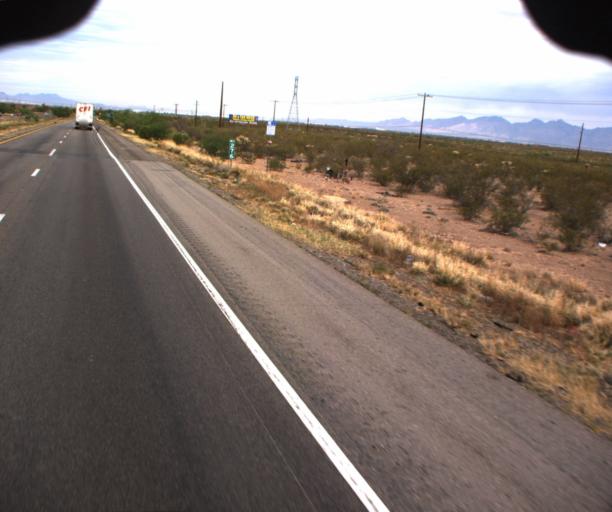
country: US
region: Arizona
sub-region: Pima County
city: Vail
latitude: 32.0571
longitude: -110.7663
